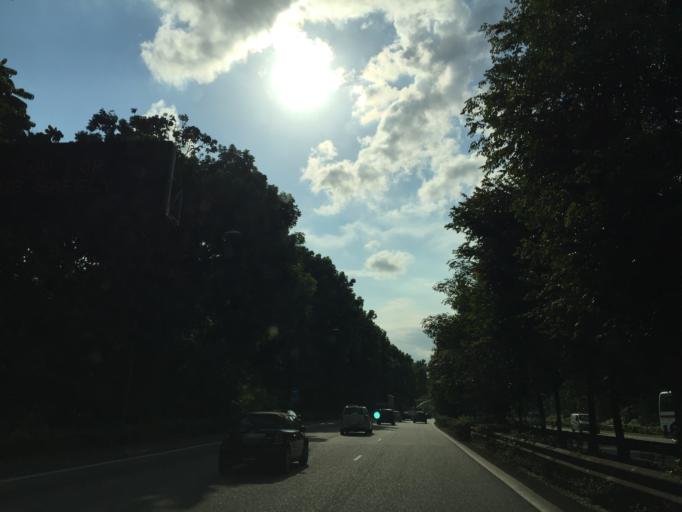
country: SG
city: Singapore
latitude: 1.3545
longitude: 103.7862
